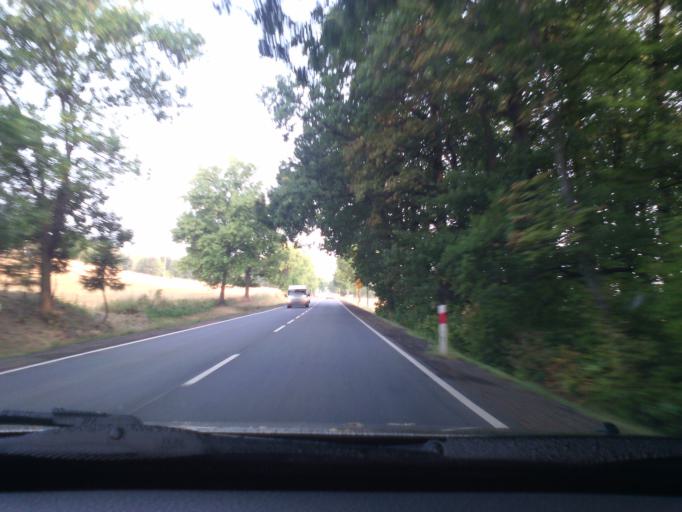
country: PL
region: Lower Silesian Voivodeship
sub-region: Powiat swidnicki
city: Swiebodzice
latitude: 50.8791
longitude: 16.2786
